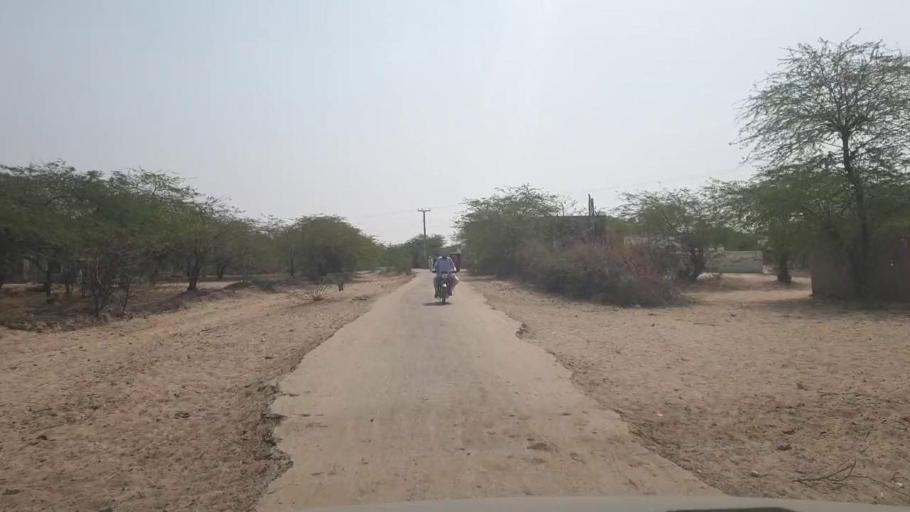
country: PK
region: Sindh
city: Chor
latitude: 25.4763
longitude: 69.7808
